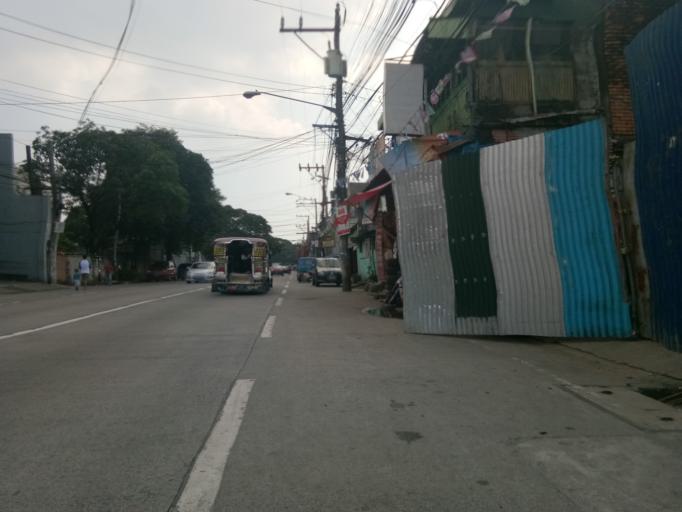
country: PH
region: Metro Manila
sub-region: Marikina
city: Calumpang
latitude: 14.6158
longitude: 121.0652
